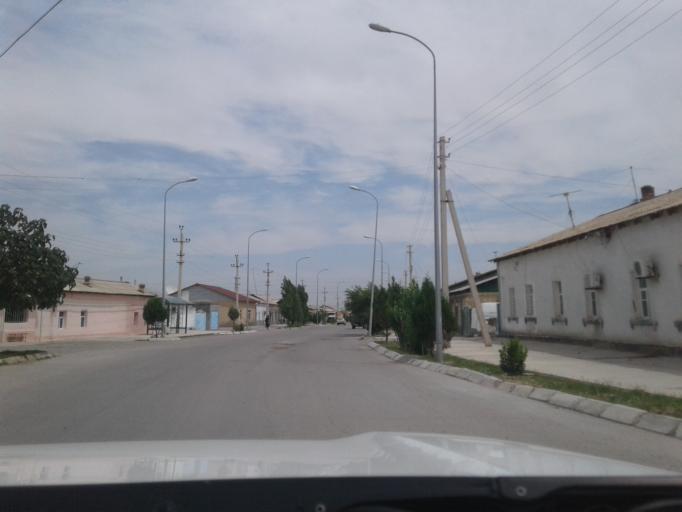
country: TM
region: Balkan
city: Serdar
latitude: 38.9716
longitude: 56.2751
